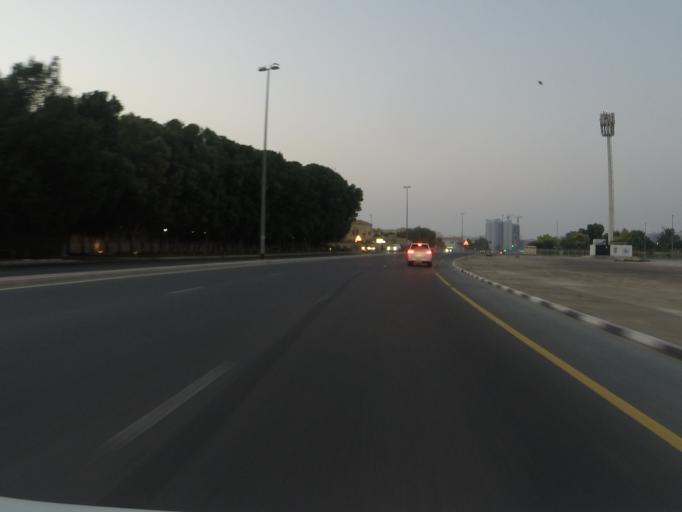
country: AE
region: Dubai
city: Dubai
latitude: 25.0987
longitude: 55.2001
